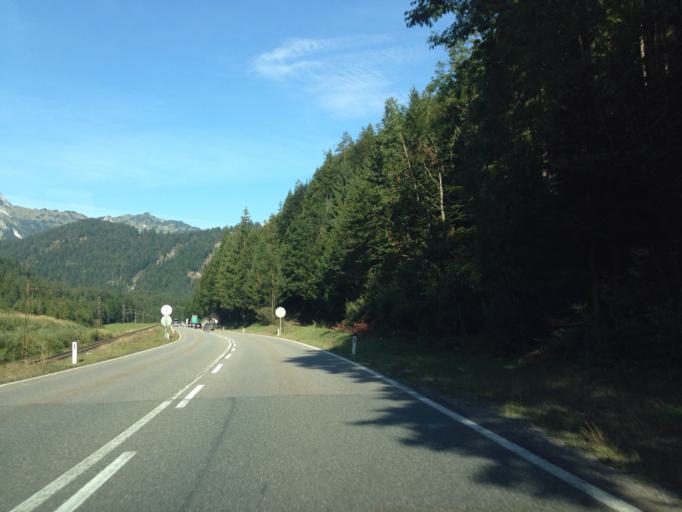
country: AT
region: Tyrol
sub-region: Politischer Bezirk Reutte
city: Heiterwang
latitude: 47.4541
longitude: 10.7305
